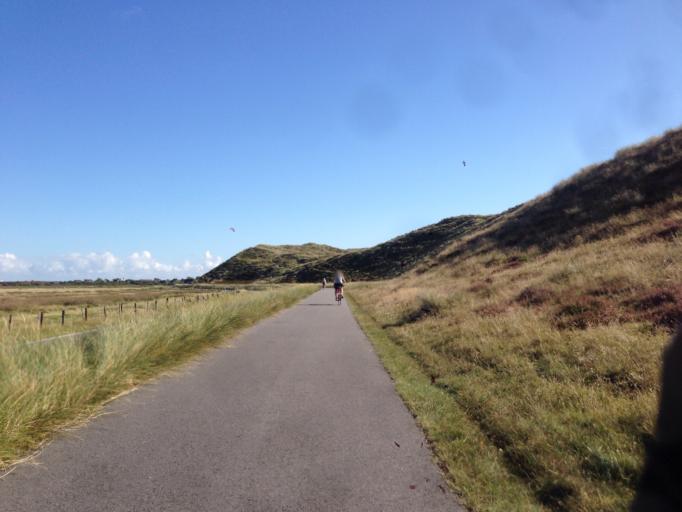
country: DE
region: Schleswig-Holstein
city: List
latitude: 55.0311
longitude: 8.4142
